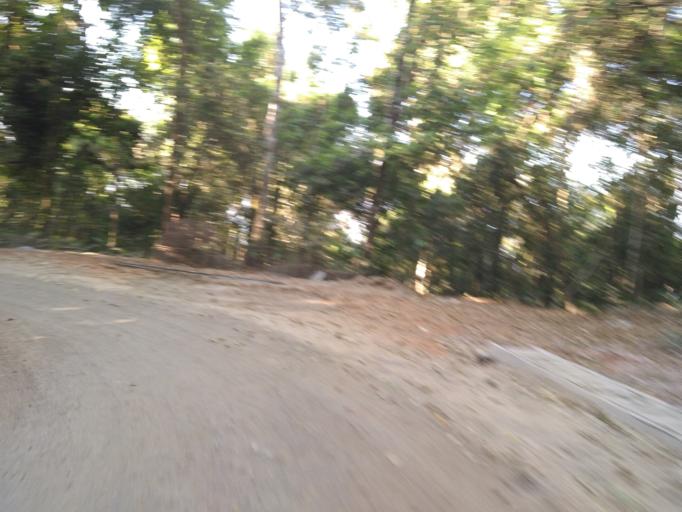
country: TH
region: Chiang Mai
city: Chiang Mai
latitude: 18.8144
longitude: 98.8885
